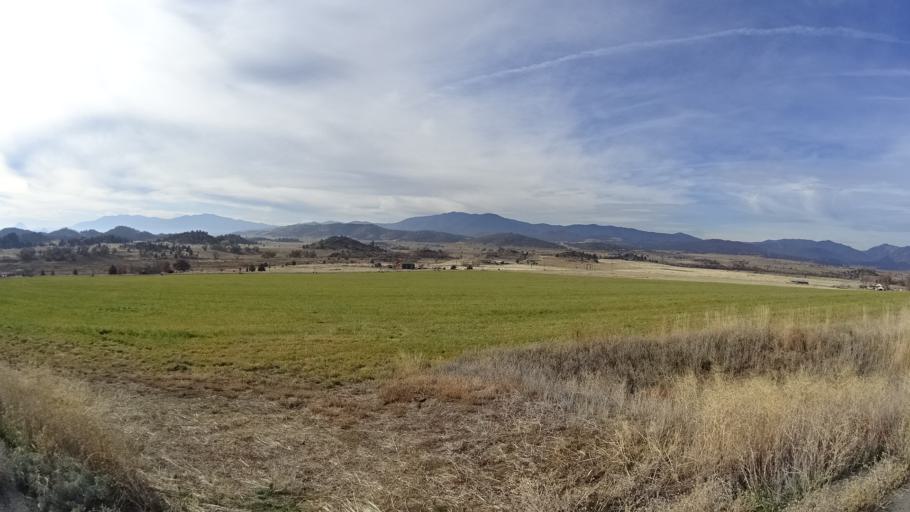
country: US
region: California
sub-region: Siskiyou County
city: Montague
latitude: 41.7082
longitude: -122.5170
